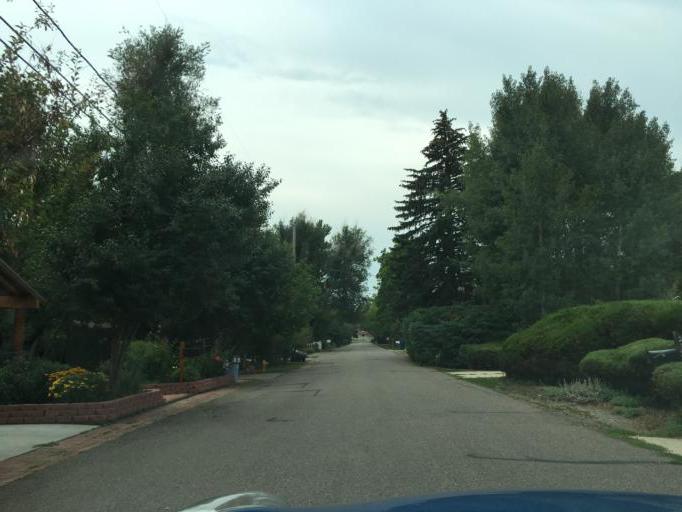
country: US
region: Colorado
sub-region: Jefferson County
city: Wheat Ridge
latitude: 39.7498
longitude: -105.0964
